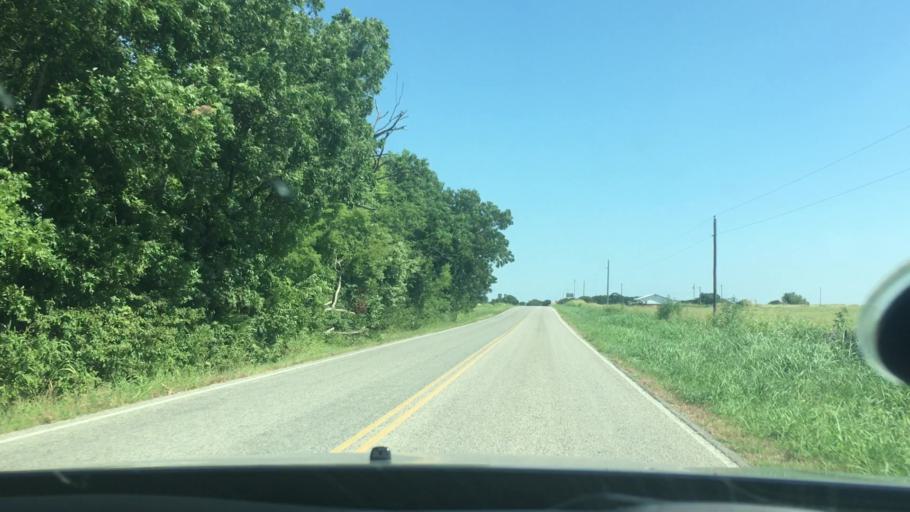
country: US
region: Oklahoma
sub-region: Johnston County
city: Tishomingo
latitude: 34.3072
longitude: -96.6184
